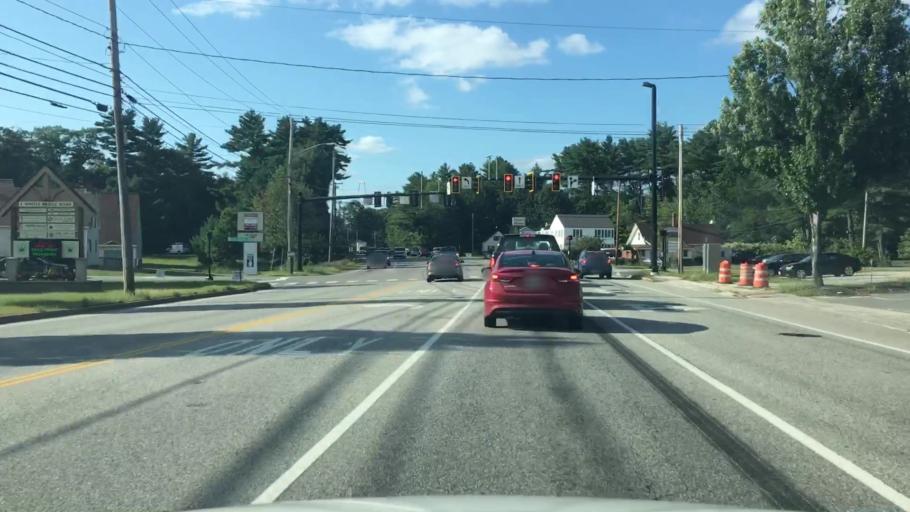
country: US
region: Maine
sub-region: Cumberland County
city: North Windham
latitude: 43.8483
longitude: -70.4484
